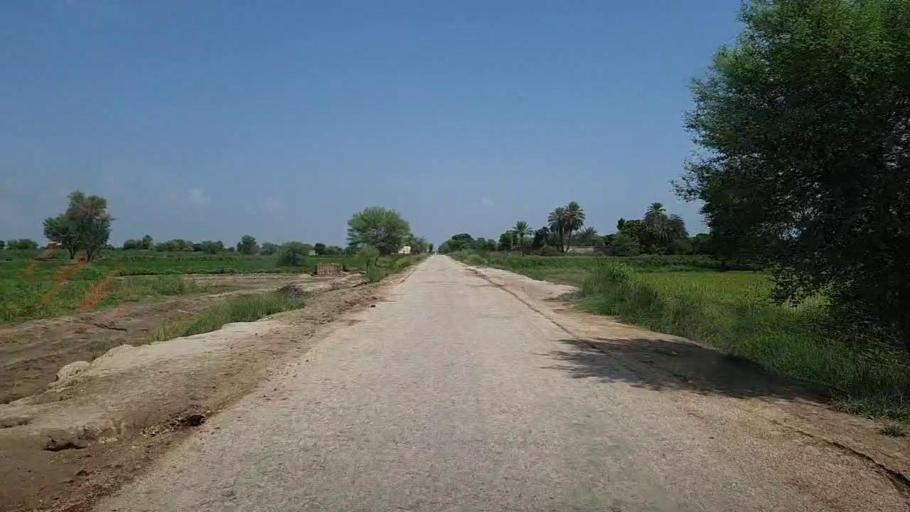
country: PK
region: Sindh
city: Bhiria
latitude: 26.8886
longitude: 68.2305
